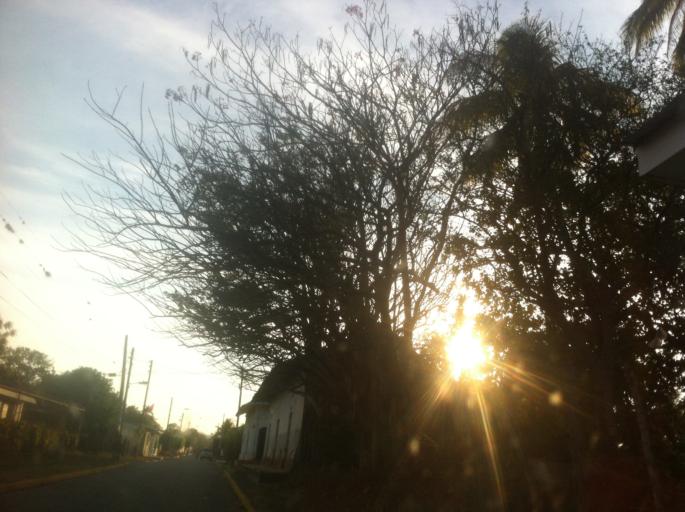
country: NI
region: Rivas
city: Potosi
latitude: 11.4950
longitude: -85.8563
